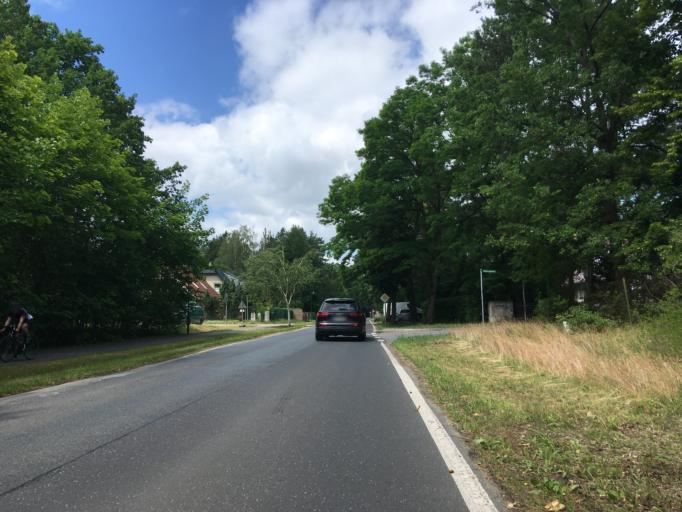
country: DE
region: Brandenburg
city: Wandlitz
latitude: 52.7699
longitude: 13.4547
